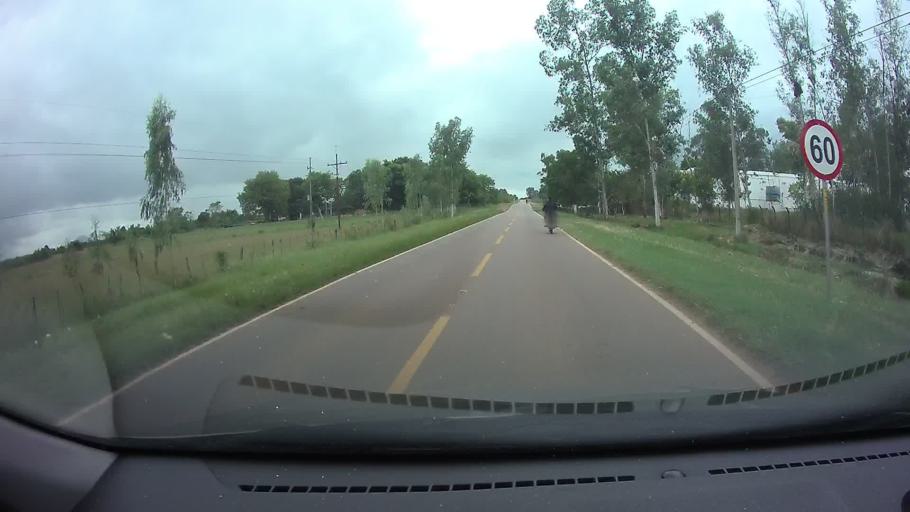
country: PY
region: Paraguari
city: Carapegua
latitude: -25.7741
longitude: -57.2303
